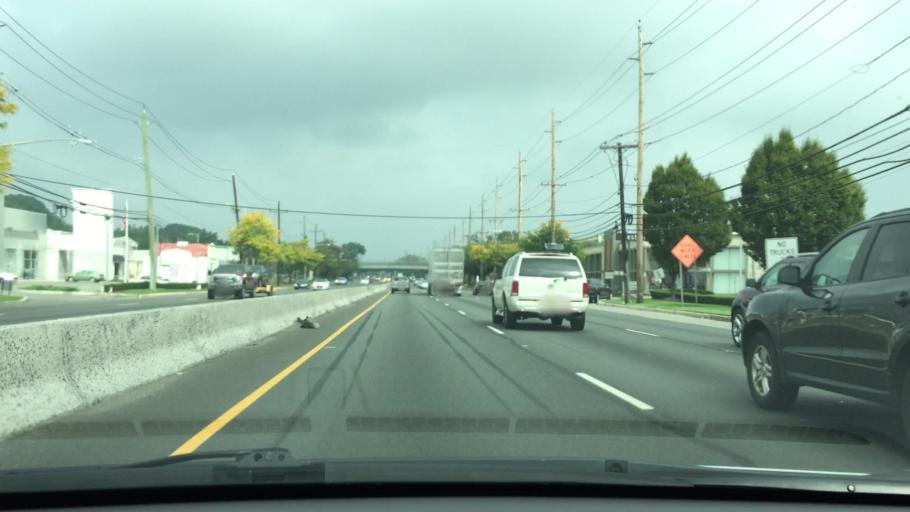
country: US
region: New Jersey
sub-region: Bergen County
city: Paramus
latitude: 40.9458
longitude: -74.0718
